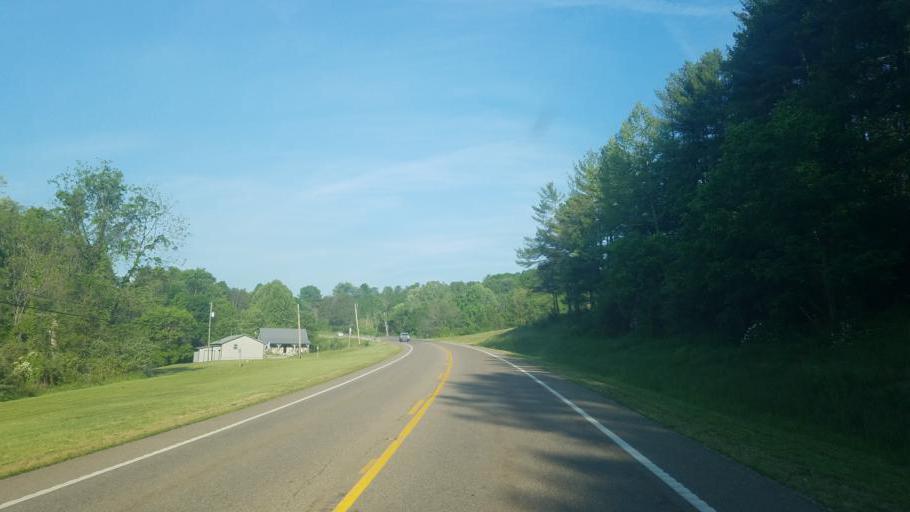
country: US
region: West Virginia
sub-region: Mason County
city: New Haven
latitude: 39.1176
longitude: -81.9072
